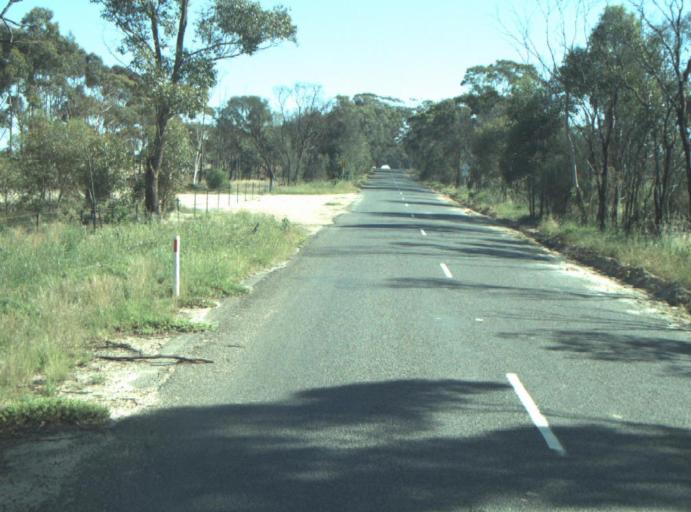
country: AU
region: Victoria
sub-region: Greater Geelong
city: Lara
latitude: -37.9229
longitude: 144.3960
